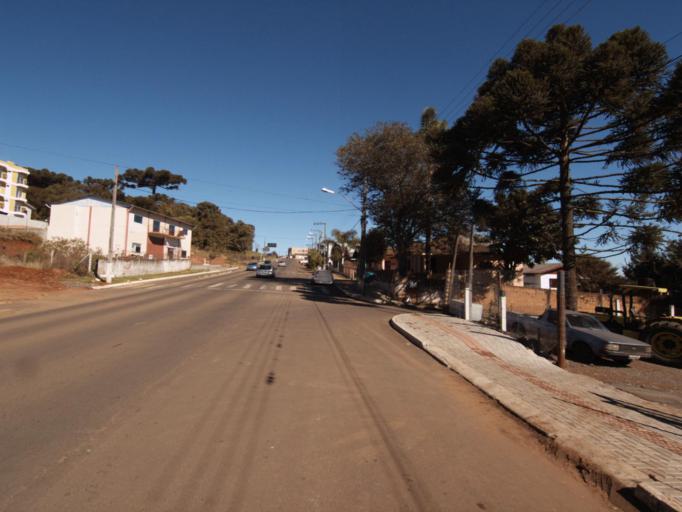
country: BR
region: Santa Catarina
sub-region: Xanxere
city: Xanxere
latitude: -26.8843
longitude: -52.4035
